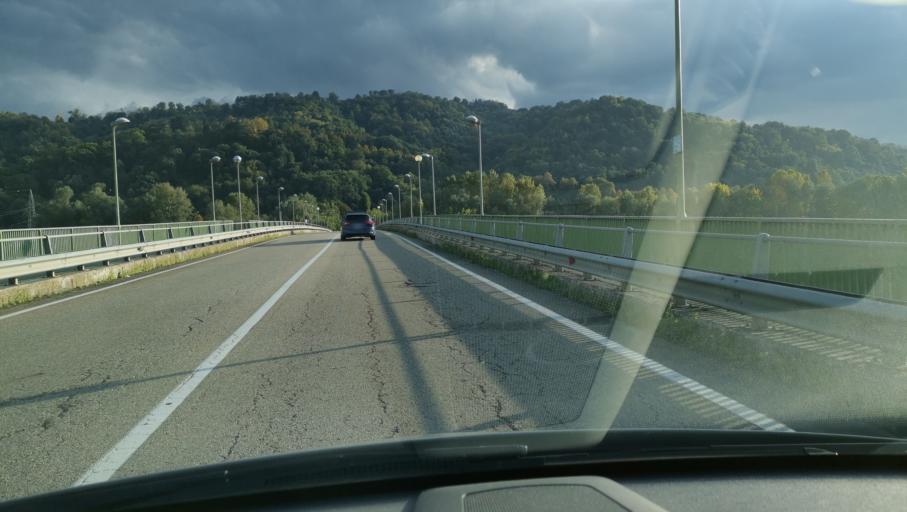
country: IT
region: Piedmont
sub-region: Provincia di Torino
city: Chivasso
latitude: 45.1819
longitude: 7.8902
